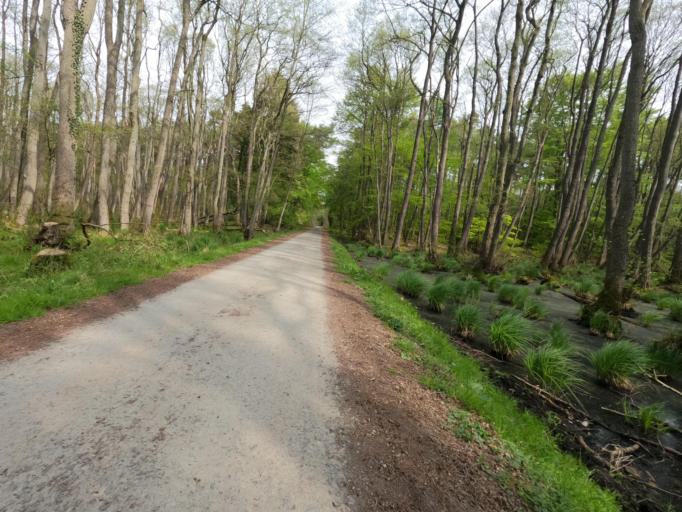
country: DE
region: Mecklenburg-Vorpommern
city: Ostseebad Prerow
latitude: 54.4554
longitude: 12.5126
